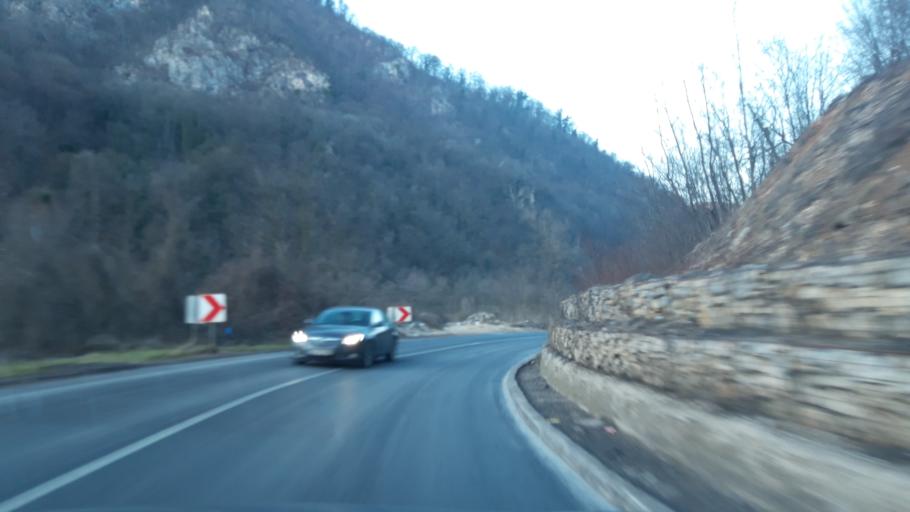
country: BA
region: Republika Srpska
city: Milici
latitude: 44.2669
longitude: 19.1033
